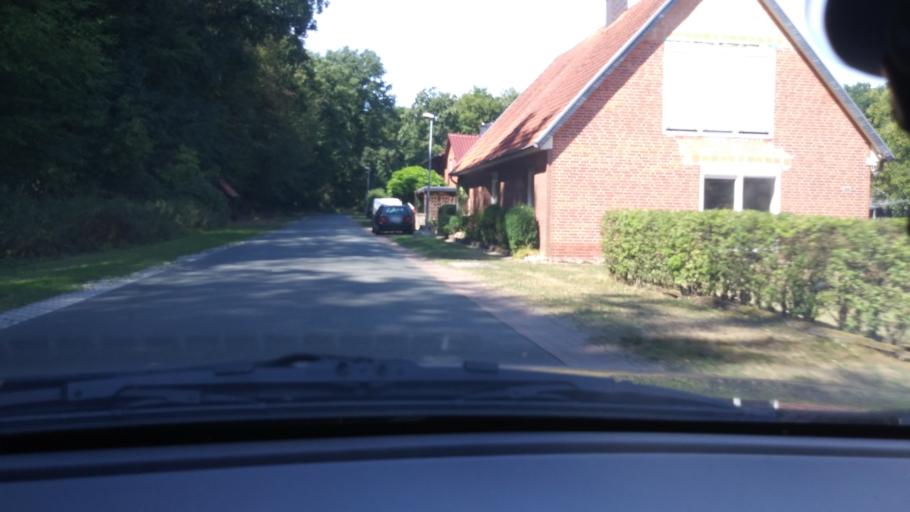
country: DE
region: Lower Saxony
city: Binnen
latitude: 52.6212
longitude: 9.1246
